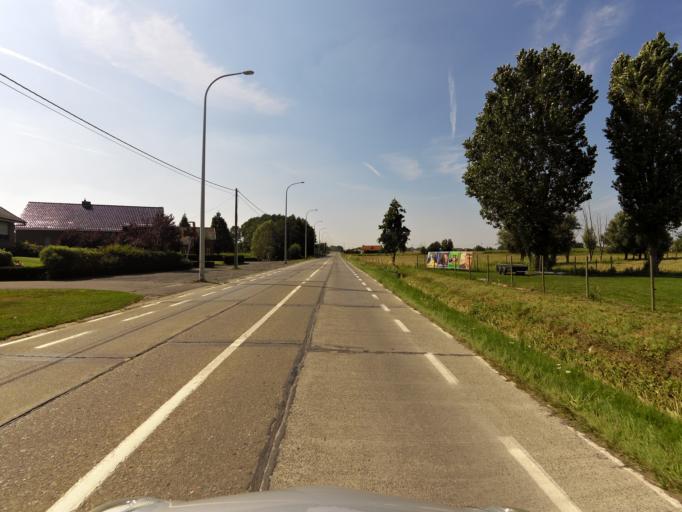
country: BE
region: Flanders
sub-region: Provincie West-Vlaanderen
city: Dentergem
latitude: 50.9886
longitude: 3.4634
